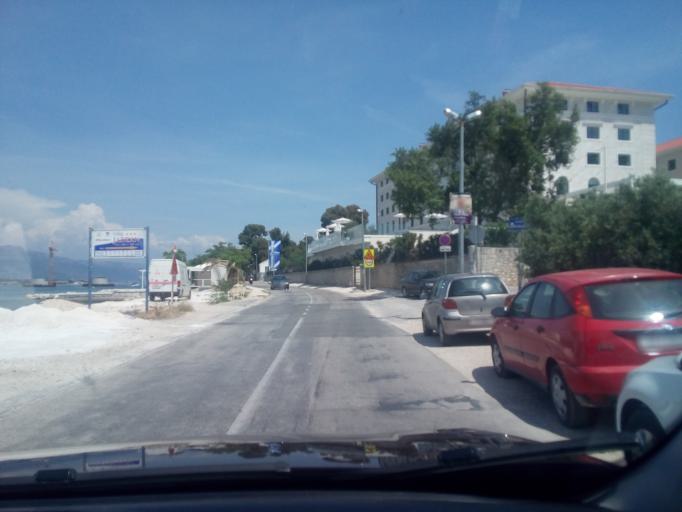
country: HR
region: Splitsko-Dalmatinska
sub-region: Grad Trogir
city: Trogir
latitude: 43.5162
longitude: 16.2583
